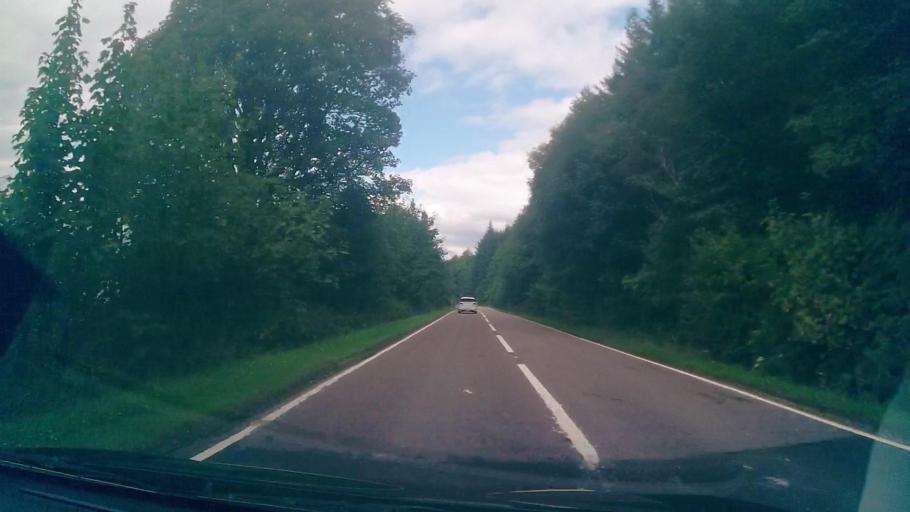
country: GB
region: Scotland
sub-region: Argyll and Bute
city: Oban
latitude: 56.4560
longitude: -5.3584
